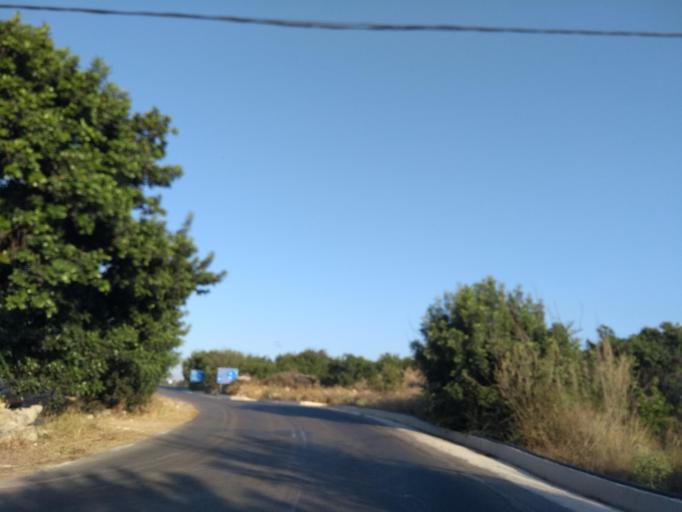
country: GR
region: Crete
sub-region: Nomos Chanias
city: Kalivai
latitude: 35.4269
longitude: 24.1811
